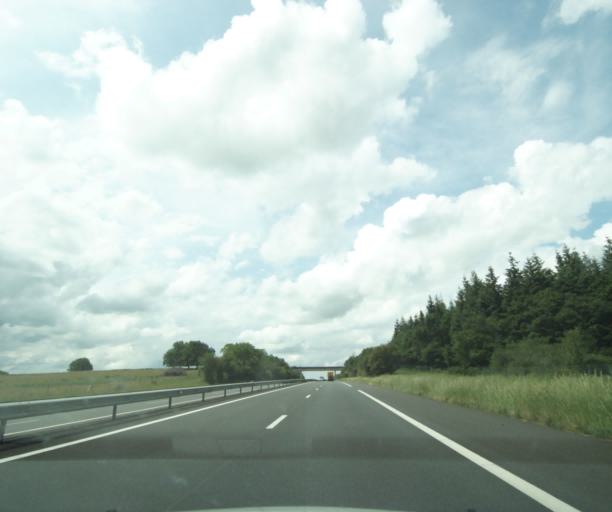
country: FR
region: Auvergne
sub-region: Departement de l'Allier
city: Bellenaves
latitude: 46.2520
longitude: 3.0828
